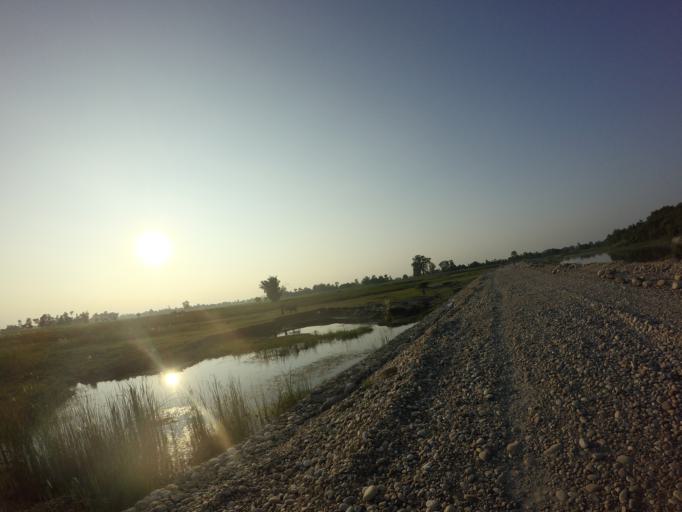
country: NP
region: Far Western
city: Tikapur
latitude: 28.4473
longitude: 81.0749
